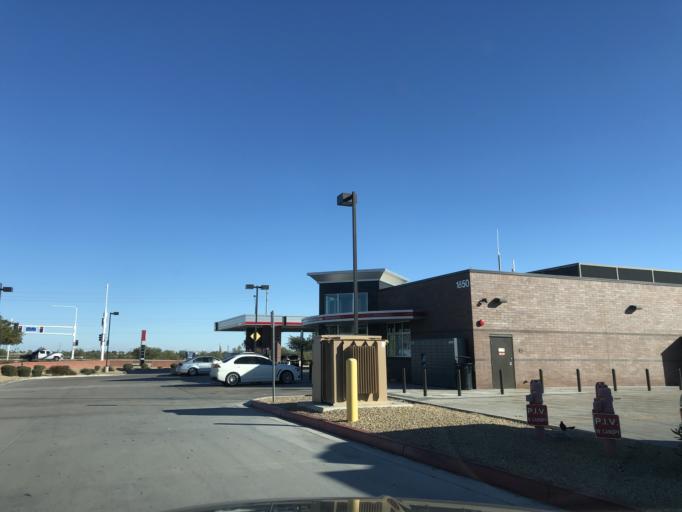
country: US
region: Arizona
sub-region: Maricopa County
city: Buckeye
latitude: 33.4298
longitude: -112.5922
